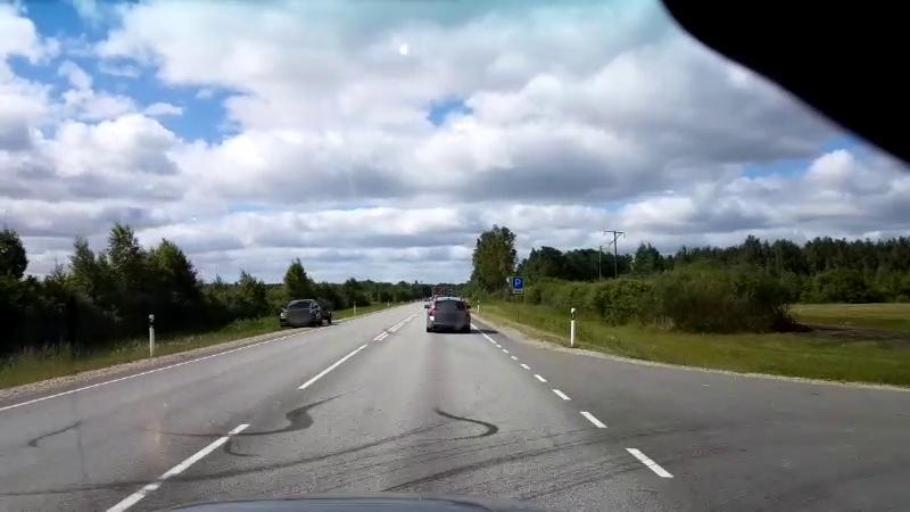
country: EE
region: Paernumaa
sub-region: Sauga vald
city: Sauga
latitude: 58.4508
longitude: 24.5044
